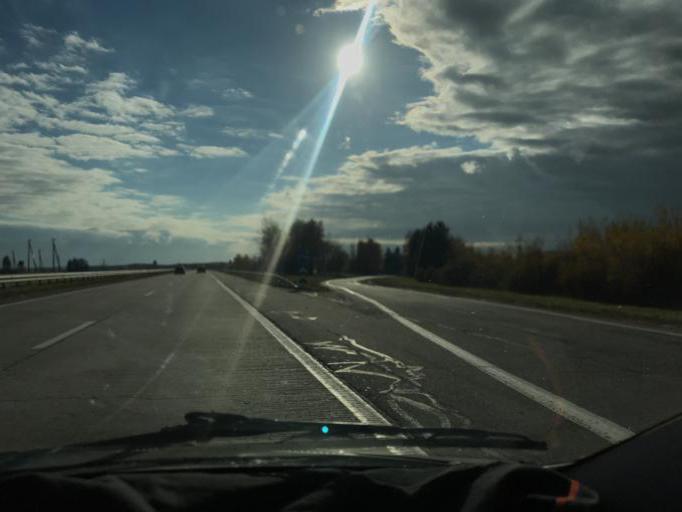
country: BY
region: Minsk
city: Lahoysk
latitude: 54.1619
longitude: 27.8148
